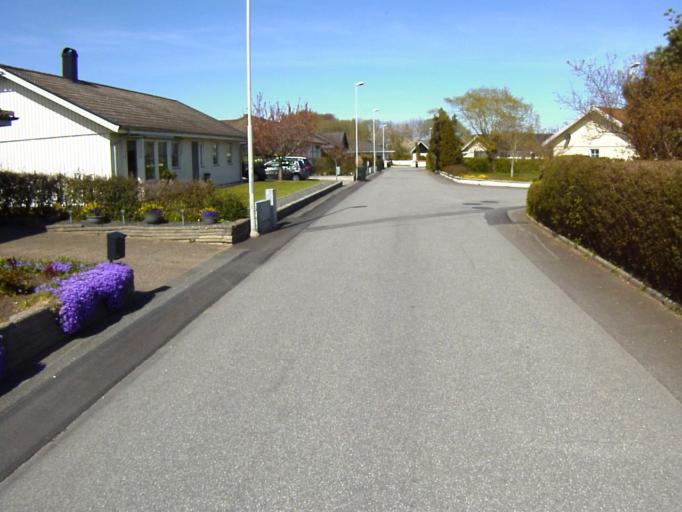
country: SE
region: Skane
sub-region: Kristianstads Kommun
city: Onnestad
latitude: 55.9989
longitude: 14.0692
